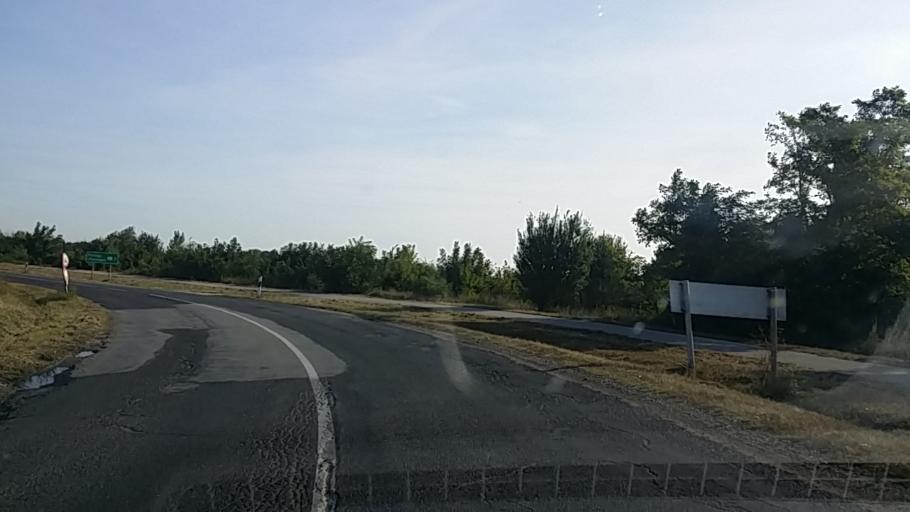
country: HU
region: Gyor-Moson-Sopron
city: Fertod
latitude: 47.6274
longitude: 16.8771
